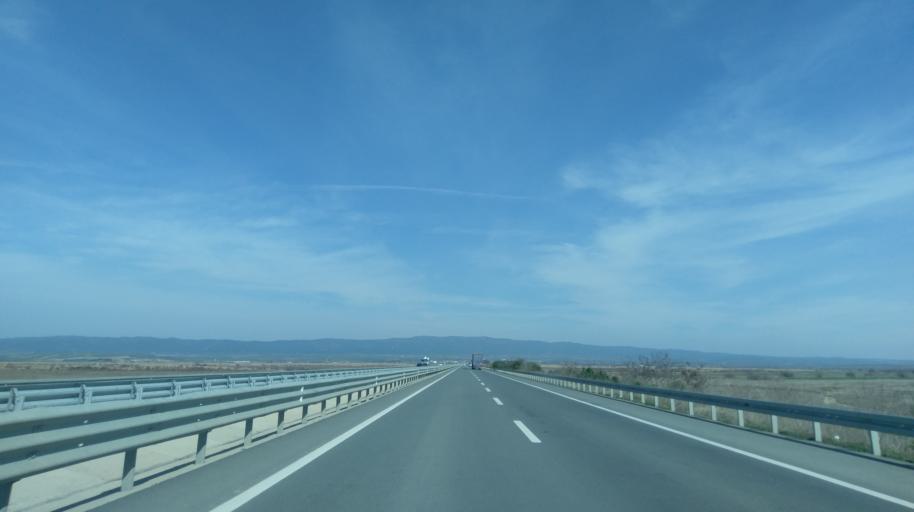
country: TR
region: Canakkale
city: Evrese
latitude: 40.6083
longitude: 26.8644
